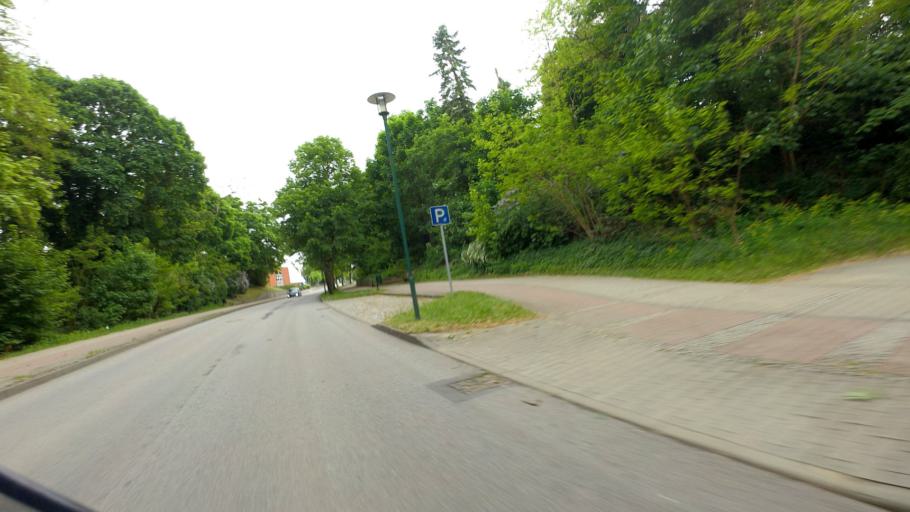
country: DE
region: Brandenburg
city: Lychen
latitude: 53.2065
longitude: 13.3196
